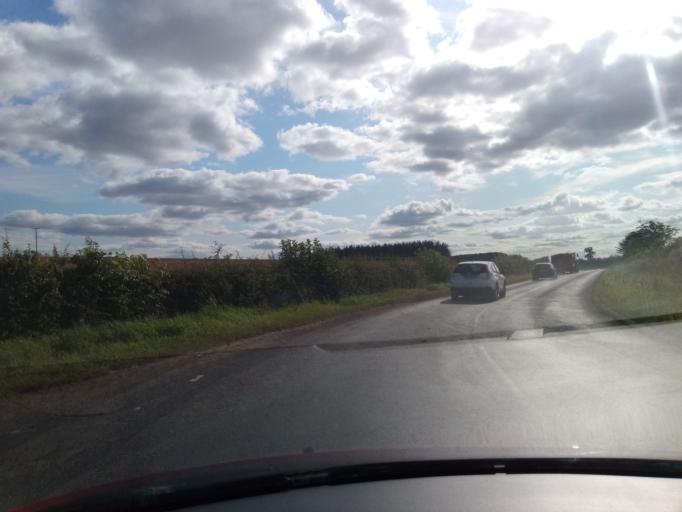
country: GB
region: Scotland
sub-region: The Scottish Borders
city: Coldstream
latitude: 55.7114
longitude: -2.2807
